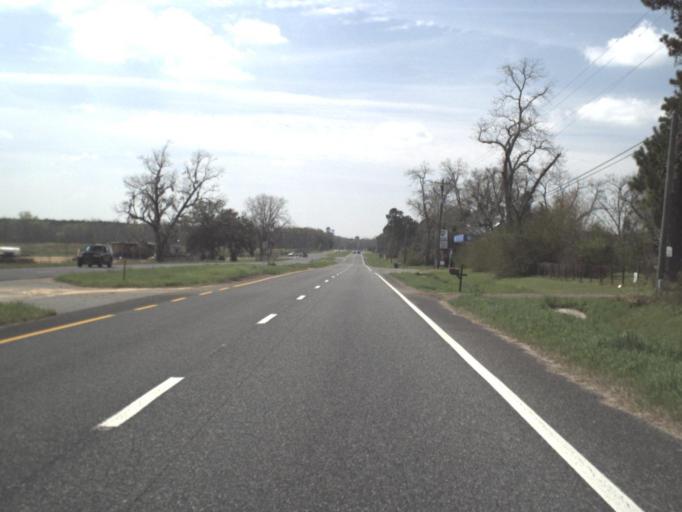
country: US
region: Florida
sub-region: Gadsden County
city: Havana
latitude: 30.6639
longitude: -84.4101
